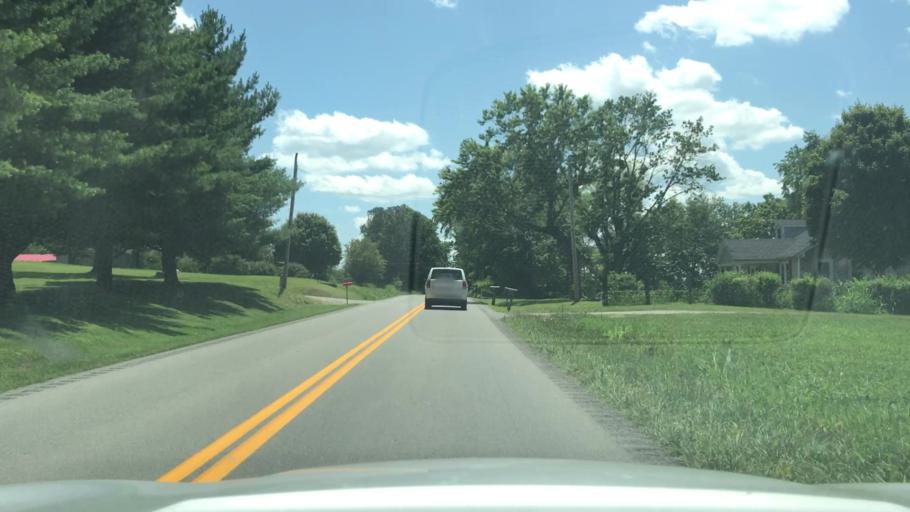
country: US
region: Kentucky
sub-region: Christian County
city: Hopkinsville
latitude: 36.9017
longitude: -87.4484
